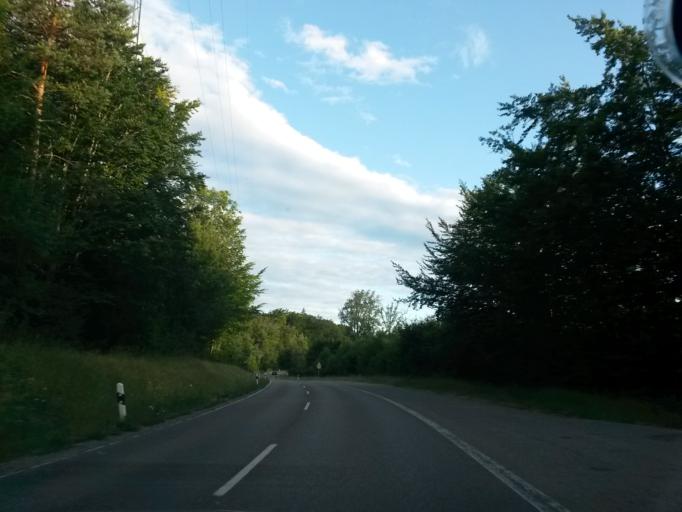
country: DE
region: Baden-Wuerttemberg
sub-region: Karlsruhe Region
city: Ispringen
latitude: 48.9091
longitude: 8.6272
